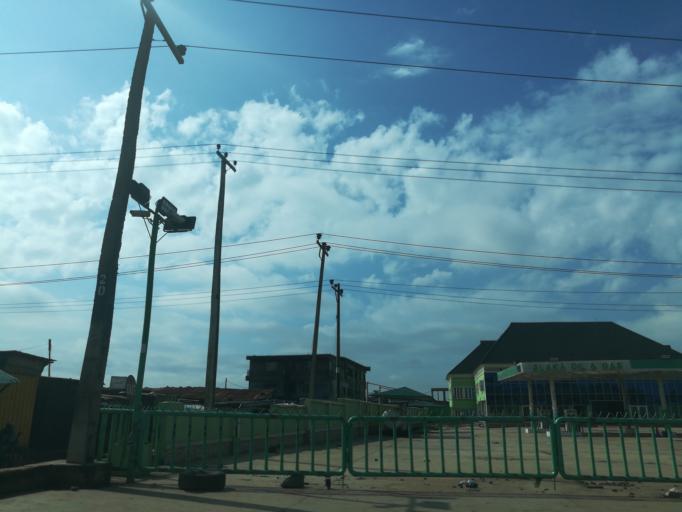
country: NG
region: Lagos
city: Ikorodu
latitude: 6.6285
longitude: 3.5101
